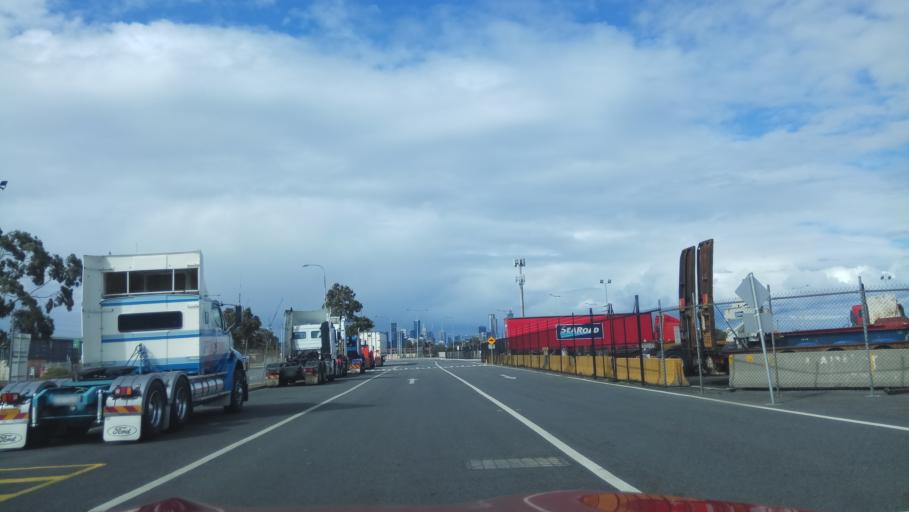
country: AU
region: Victoria
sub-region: Hobsons Bay
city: Williamstown
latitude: -37.8420
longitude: 144.9101
